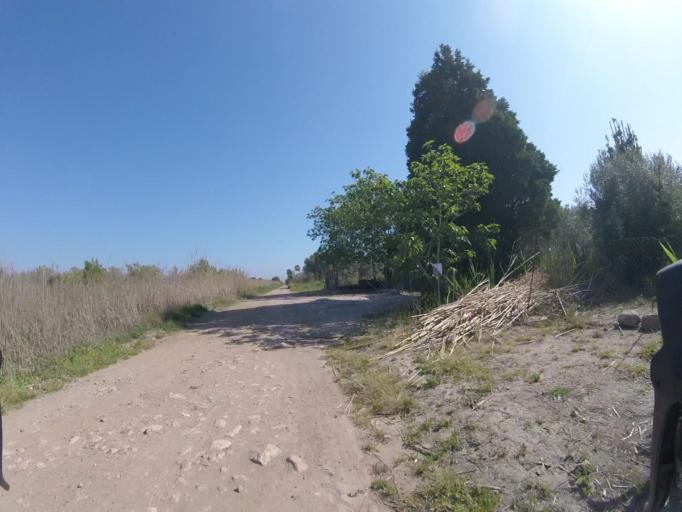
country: ES
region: Valencia
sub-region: Provincia de Castello
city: Orpesa/Oropesa del Mar
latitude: 40.1519
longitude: 0.1681
